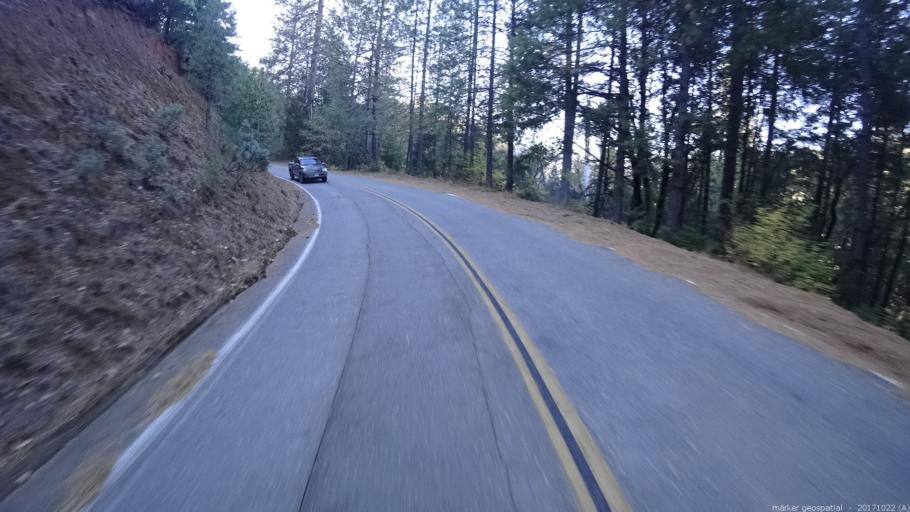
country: US
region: California
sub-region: Shasta County
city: Shasta Lake
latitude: 40.9109
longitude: -122.2368
